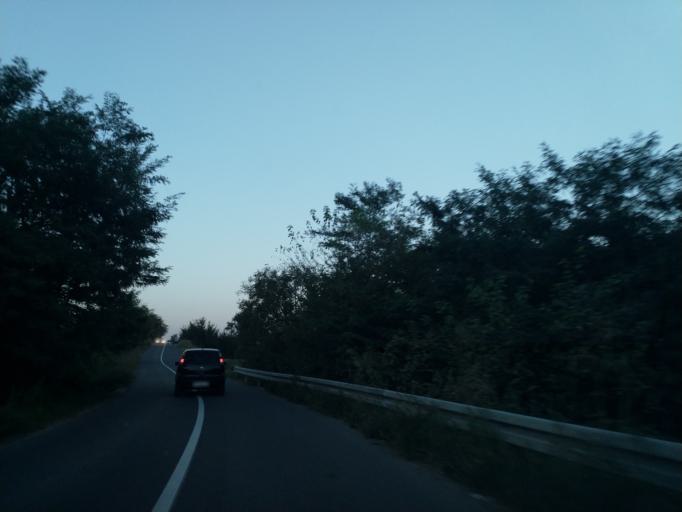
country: RS
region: Central Serbia
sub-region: Rasinski Okrug
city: Krusevac
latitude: 43.6295
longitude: 21.3717
